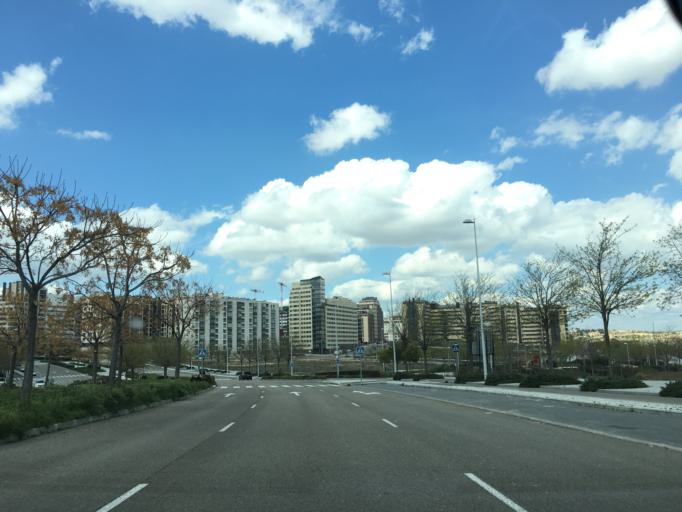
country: ES
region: Madrid
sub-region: Provincia de Madrid
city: Hortaleza
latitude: 40.4923
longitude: -3.6106
